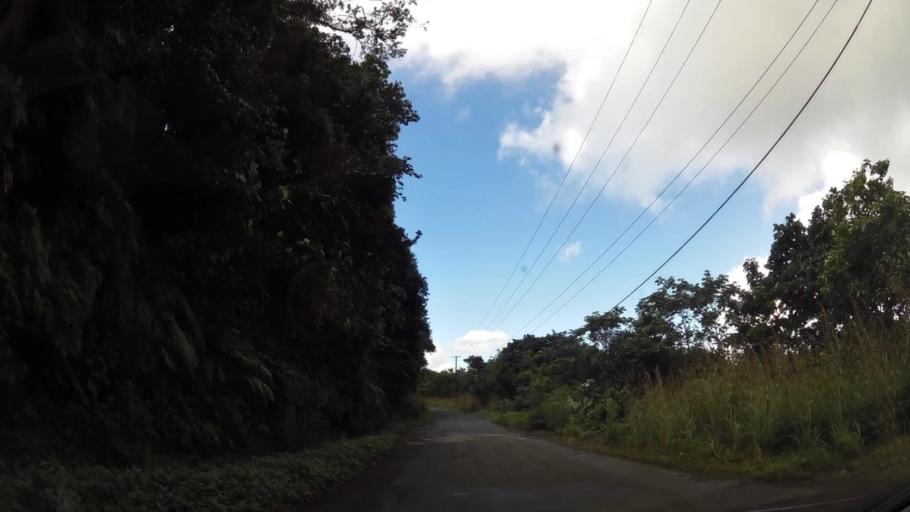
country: DM
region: Saint Paul
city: Pont Casse
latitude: 15.3919
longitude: -61.3267
